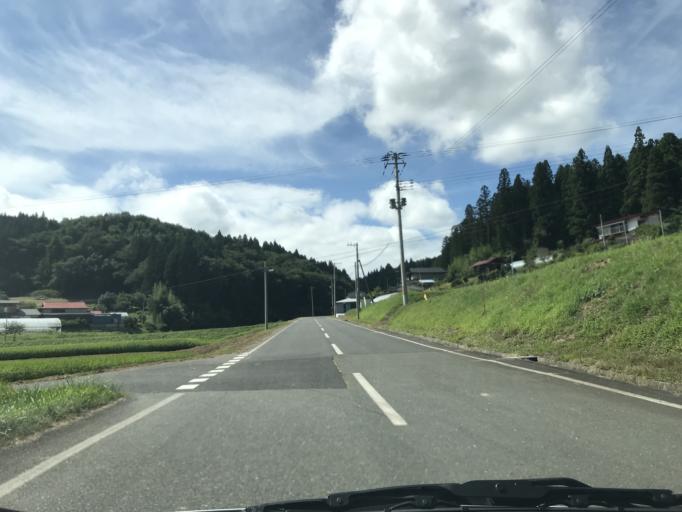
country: JP
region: Iwate
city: Ichinoseki
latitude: 38.9599
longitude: 141.0867
